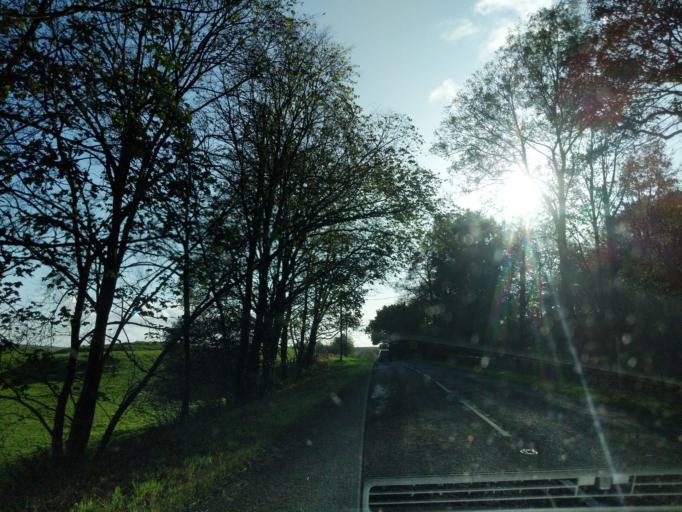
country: GB
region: Scotland
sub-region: Dumfries and Galloway
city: Kirkcudbright
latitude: 54.8829
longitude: -4.0219
